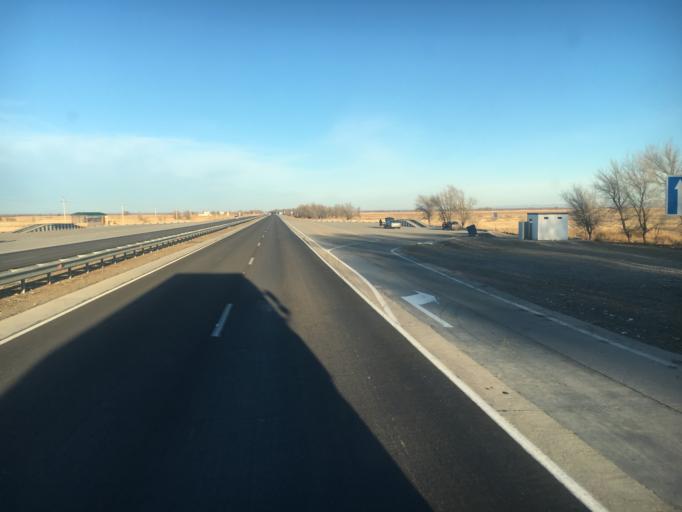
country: KZ
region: Ongtustik Qazaqstan
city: Bayaldyr
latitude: 43.0889
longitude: 68.6424
